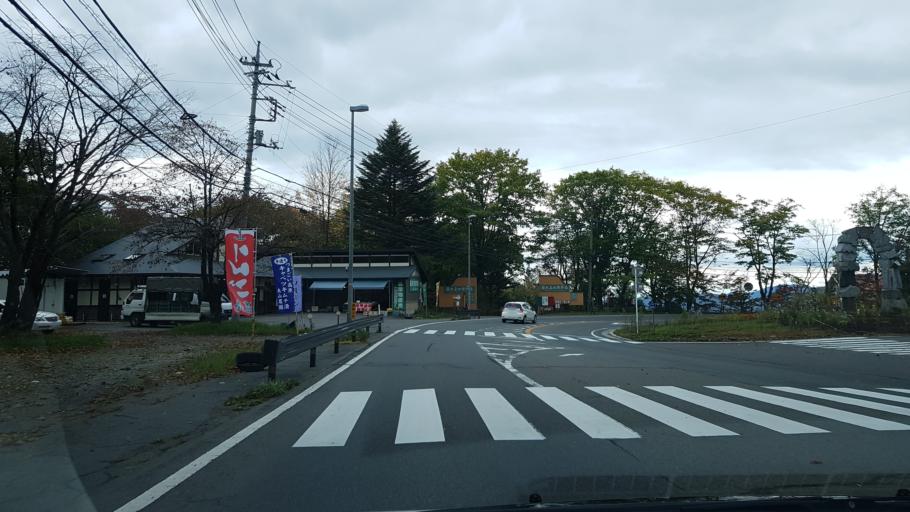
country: JP
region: Gunma
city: Nakanojomachi
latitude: 36.6086
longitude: 138.5836
